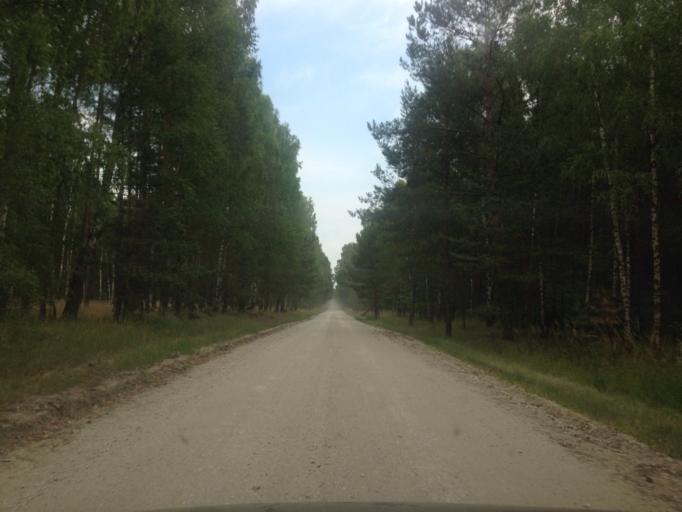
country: PL
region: Kujawsko-Pomorskie
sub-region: Powiat golubsko-dobrzynski
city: Radomin
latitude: 53.1764
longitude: 19.1836
